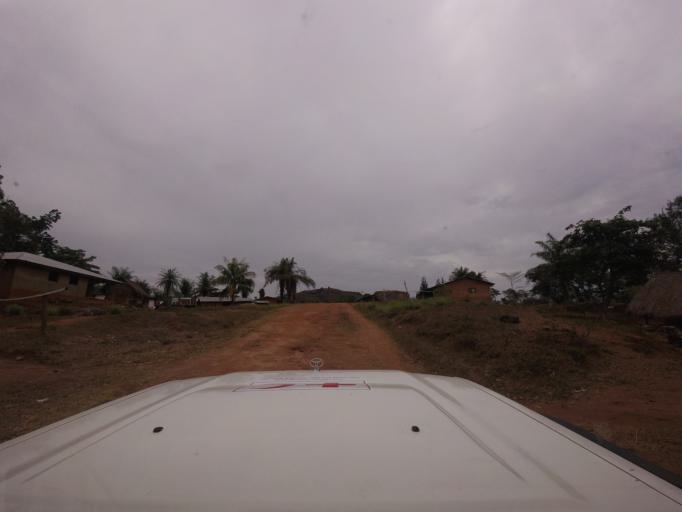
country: SL
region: Eastern Province
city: Buedu
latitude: 8.2753
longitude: -10.2789
